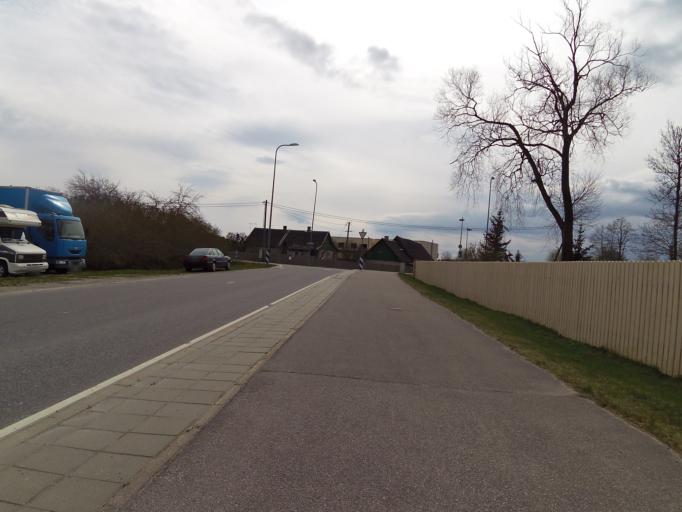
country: EE
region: Harju
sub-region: Rae vald
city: Jueri
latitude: 59.3744
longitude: 24.8428
